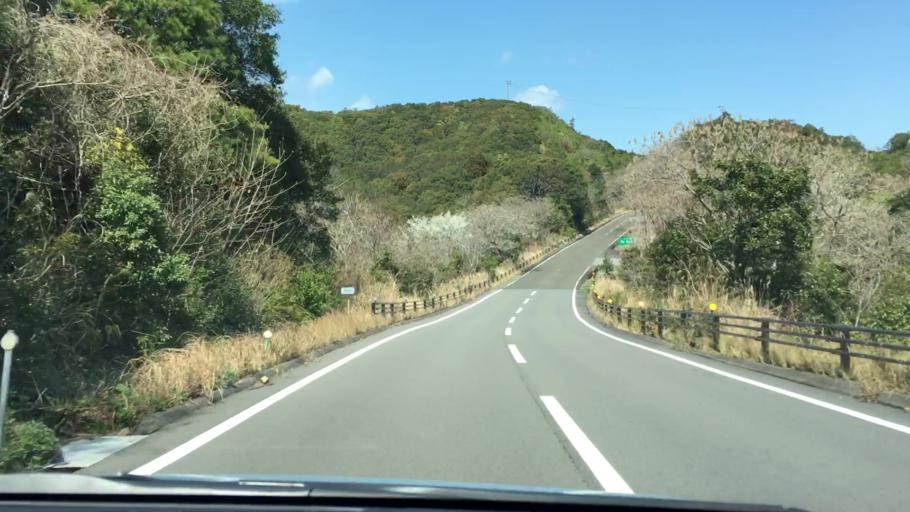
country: JP
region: Mie
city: Toba
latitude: 34.4391
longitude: 136.9111
